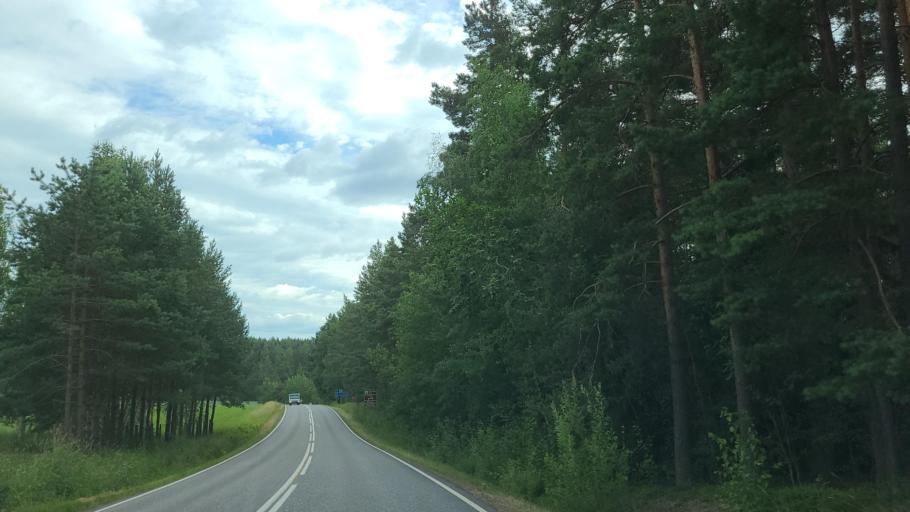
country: FI
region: Varsinais-Suomi
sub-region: Turku
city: Rymaettylae
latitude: 60.3615
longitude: 21.9531
